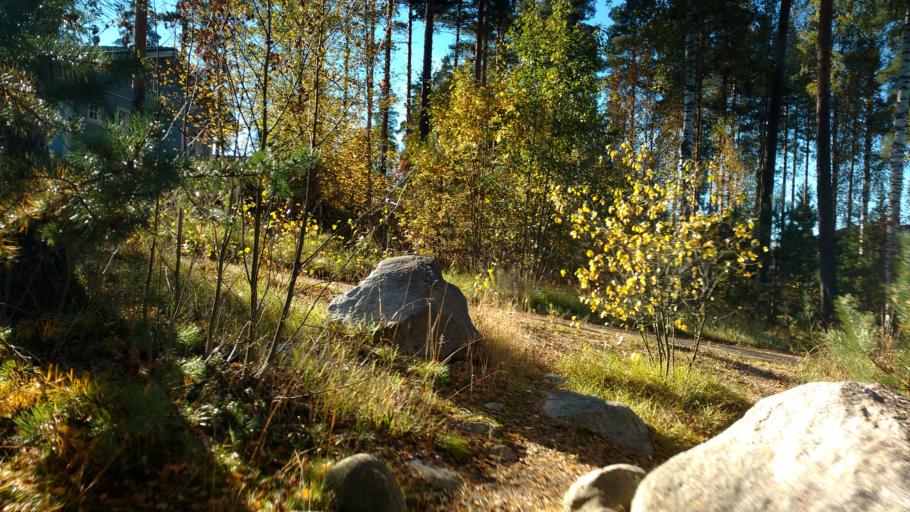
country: FI
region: Varsinais-Suomi
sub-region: Salo
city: Salo
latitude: 60.4023
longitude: 23.1846
